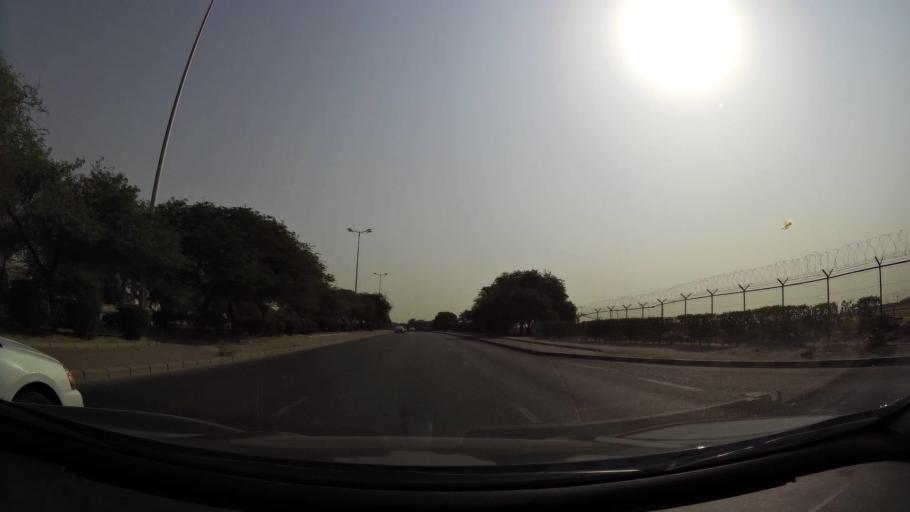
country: KW
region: Al Asimah
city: Ar Rabiyah
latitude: 29.2749
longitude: 47.8524
